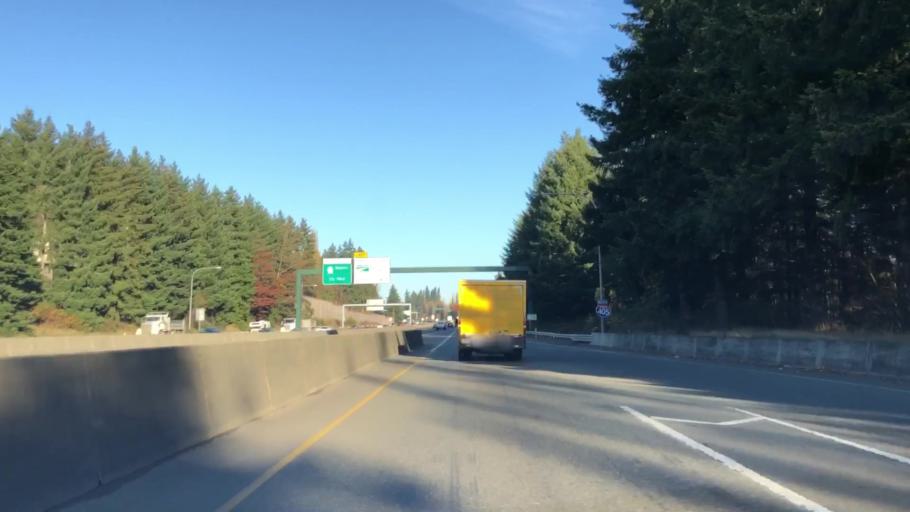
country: US
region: Washington
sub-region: King County
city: Bothell
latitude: 47.7711
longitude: -122.1896
